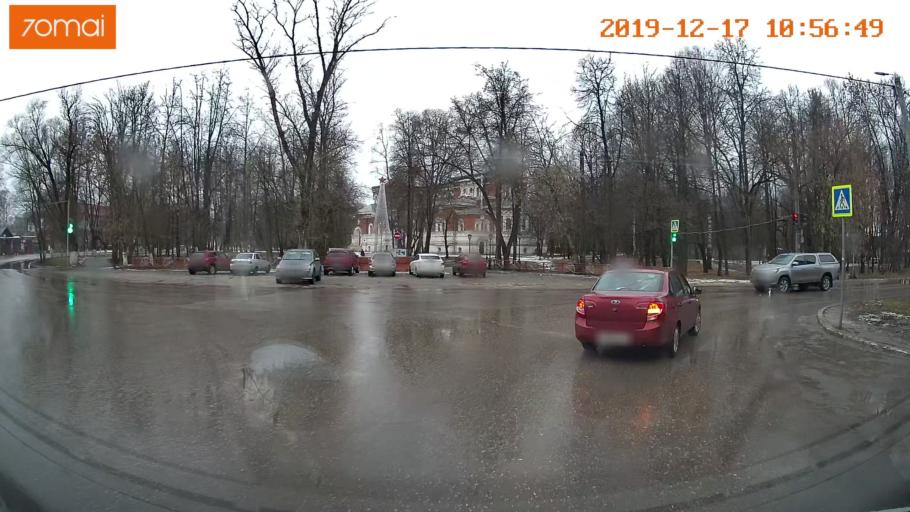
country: RU
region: Vladimir
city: Gus'-Khrustal'nyy
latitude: 55.6191
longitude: 40.6600
